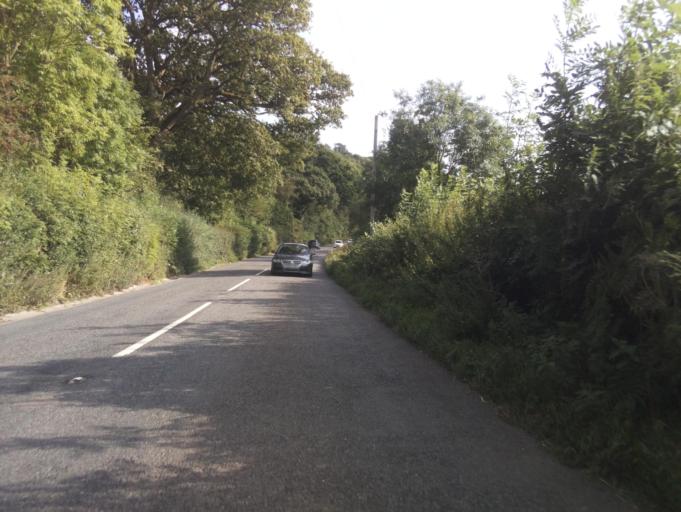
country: GB
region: England
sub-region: Devon
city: Tiverton
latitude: 50.8453
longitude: -3.5029
